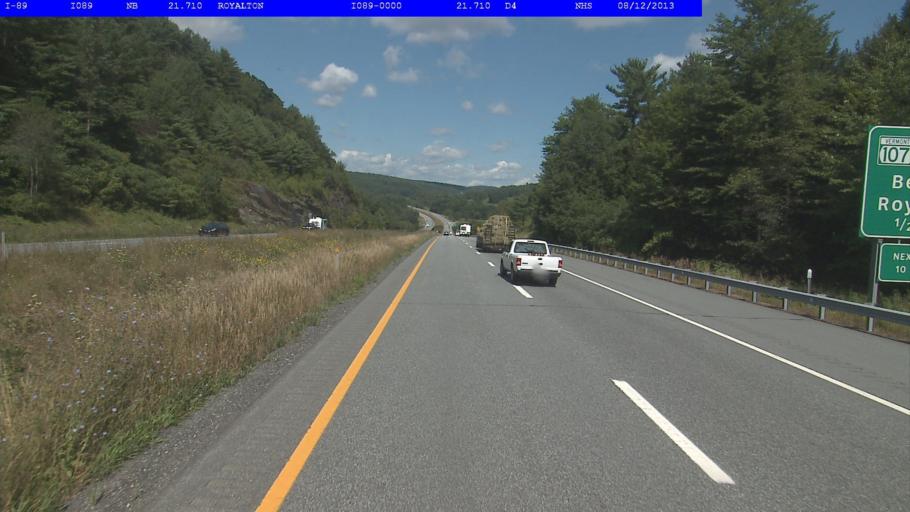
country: US
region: Vermont
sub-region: Orange County
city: Randolph
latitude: 43.8205
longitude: -72.5731
